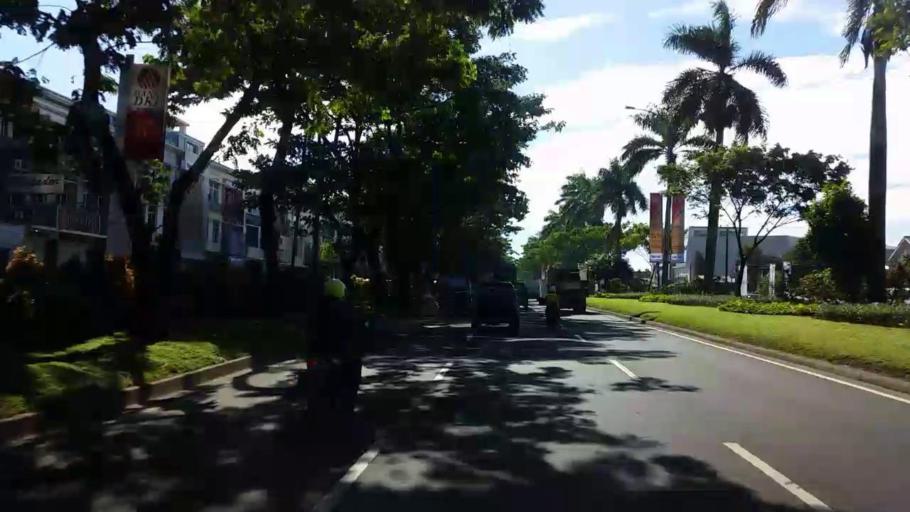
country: ID
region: West Java
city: Serpong
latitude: -6.3056
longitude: 106.6703
